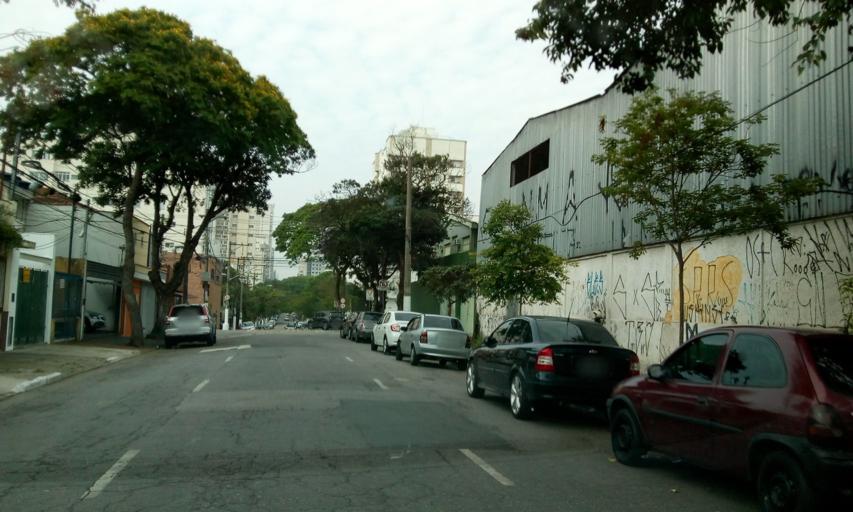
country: BR
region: Sao Paulo
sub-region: Sao Paulo
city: Sao Paulo
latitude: -23.6150
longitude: -46.6622
